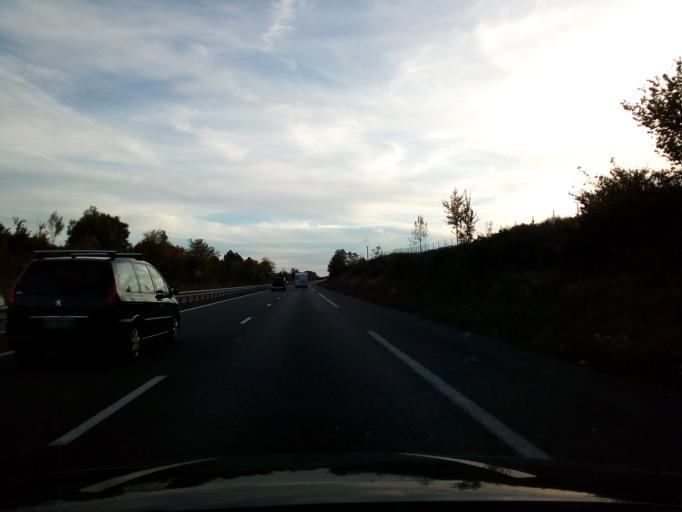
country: FR
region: Poitou-Charentes
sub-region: Departement de la Charente-Maritime
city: Montlieu-la-Garde
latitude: 45.2680
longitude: -0.2475
